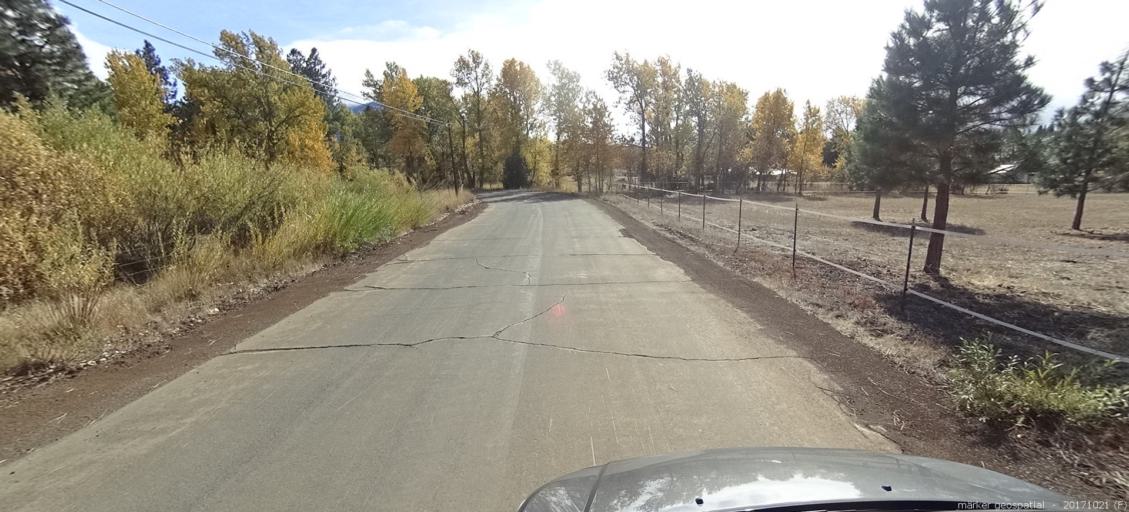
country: US
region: California
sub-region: Shasta County
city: Burney
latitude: 40.8869
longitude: -121.6691
